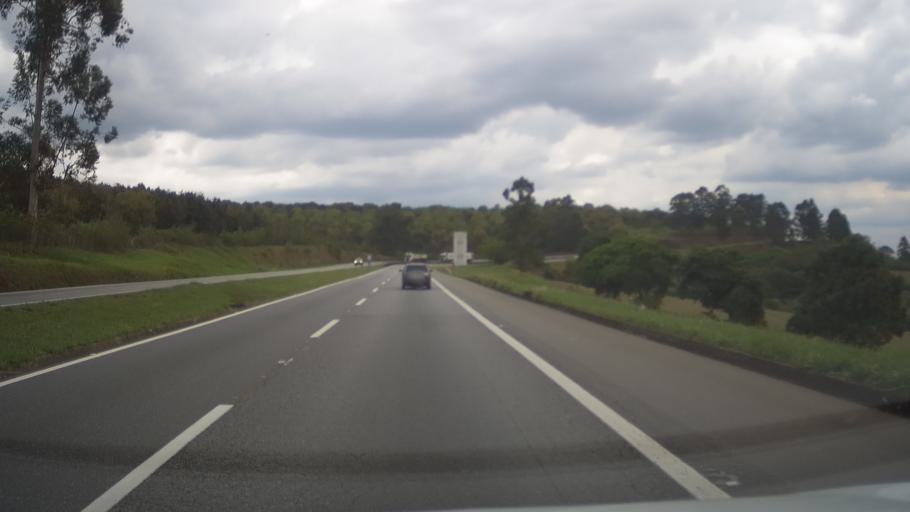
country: BR
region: Minas Gerais
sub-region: Tres Coracoes
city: Tres Coracoes
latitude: -21.5044
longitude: -45.2150
